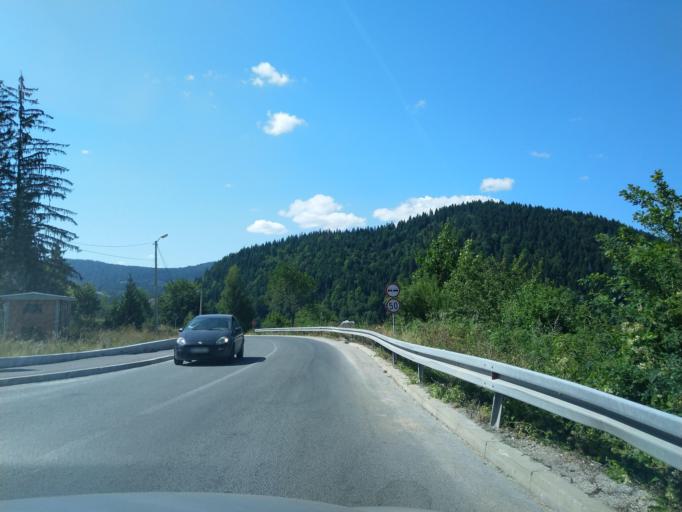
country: RS
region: Central Serbia
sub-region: Zlatiborski Okrug
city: Nova Varos
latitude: 43.4430
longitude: 19.8202
